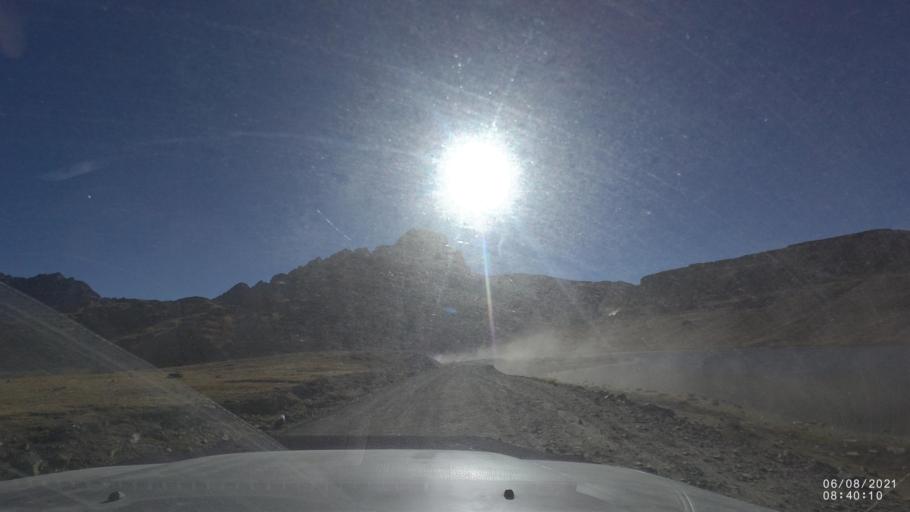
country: BO
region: Cochabamba
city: Sipe Sipe
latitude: -17.1738
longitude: -66.4006
